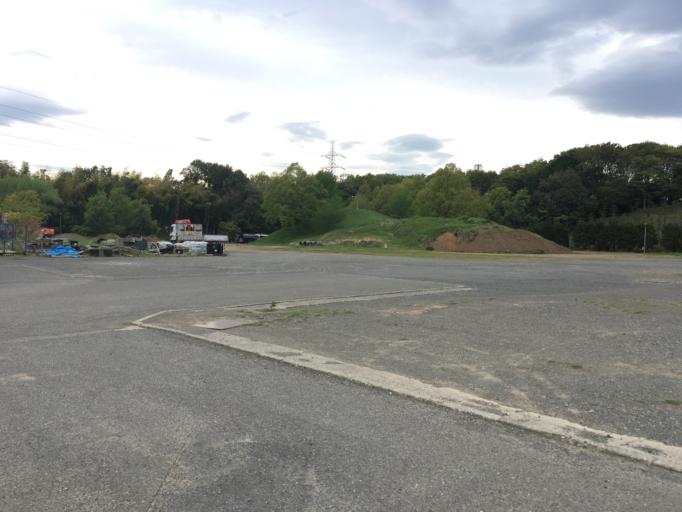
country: JP
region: Tokyo
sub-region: Machida-shi
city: Machida
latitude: 35.5697
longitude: 139.4807
